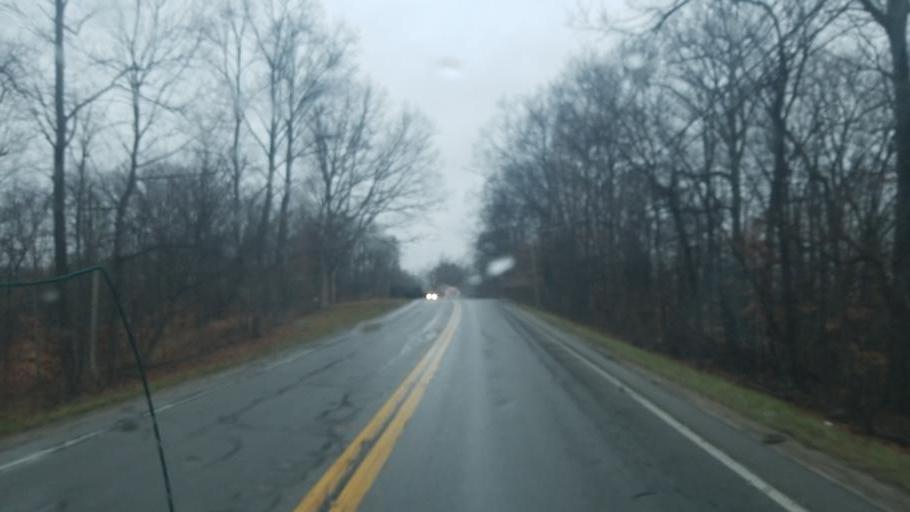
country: US
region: Indiana
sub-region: Brown County
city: Nashville
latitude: 39.1738
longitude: -86.2728
